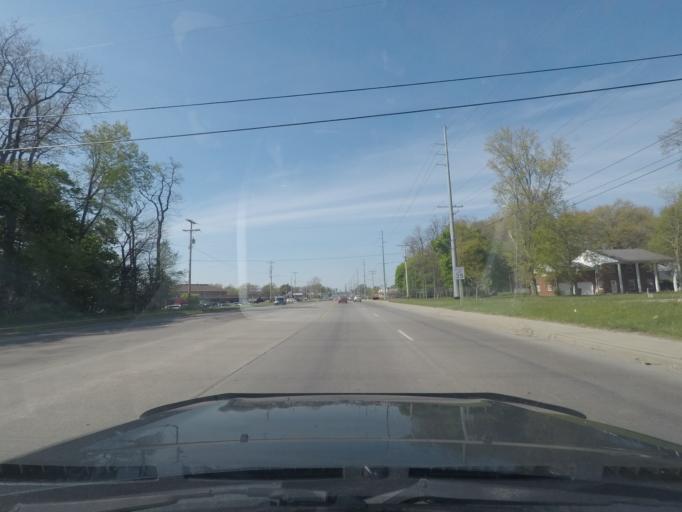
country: US
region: Indiana
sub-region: Elkhart County
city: Elkhart
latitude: 41.6806
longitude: -86.0034
